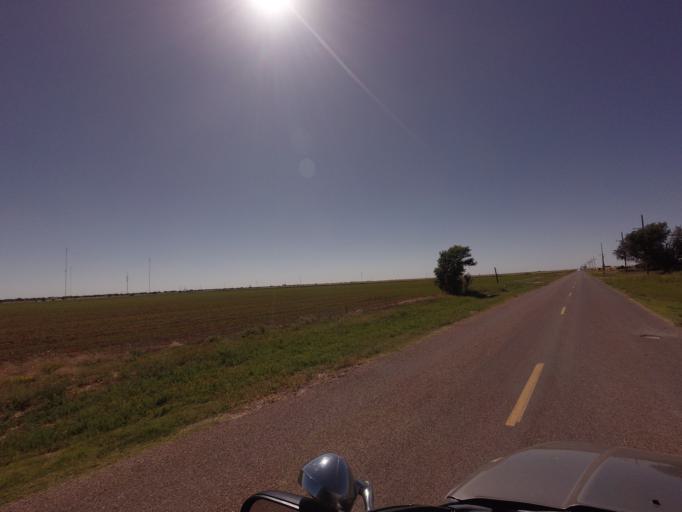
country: US
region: New Mexico
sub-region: Curry County
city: Clovis
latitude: 34.4484
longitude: -103.2101
